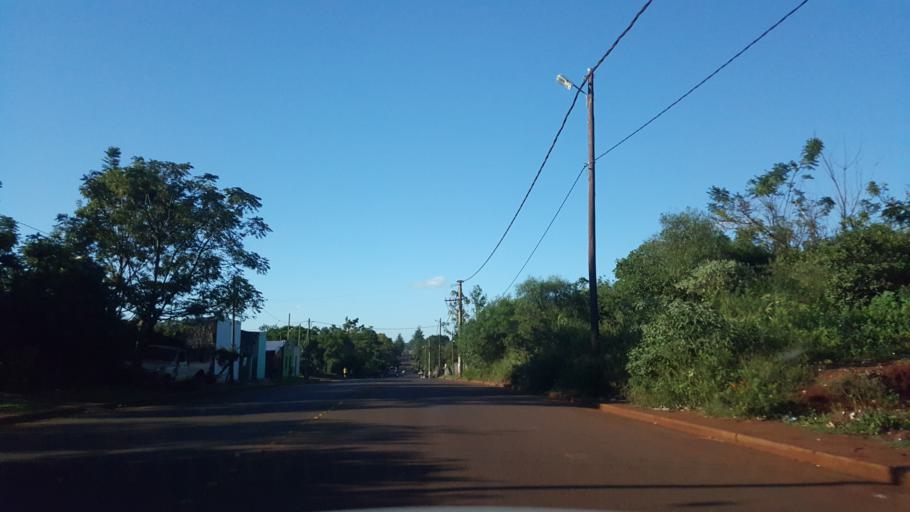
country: AR
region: Misiones
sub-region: Departamento de Capital
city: Posadas
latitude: -27.4245
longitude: -55.9591
